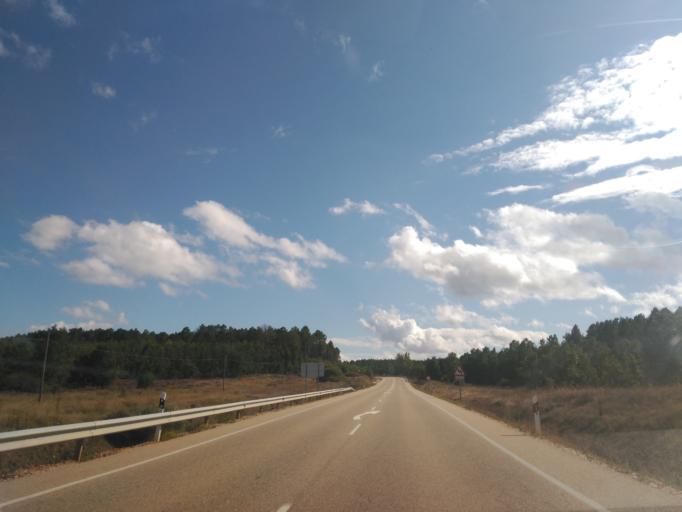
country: ES
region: Castille and Leon
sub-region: Provincia de Burgos
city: Pinilla de los Barruecos
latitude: 41.9491
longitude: -3.2918
